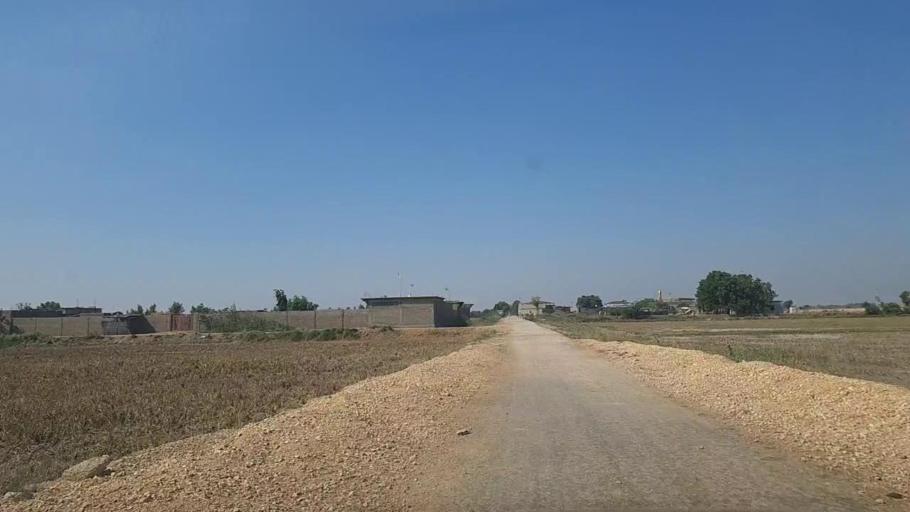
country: PK
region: Sindh
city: Thatta
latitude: 24.7687
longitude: 67.9429
